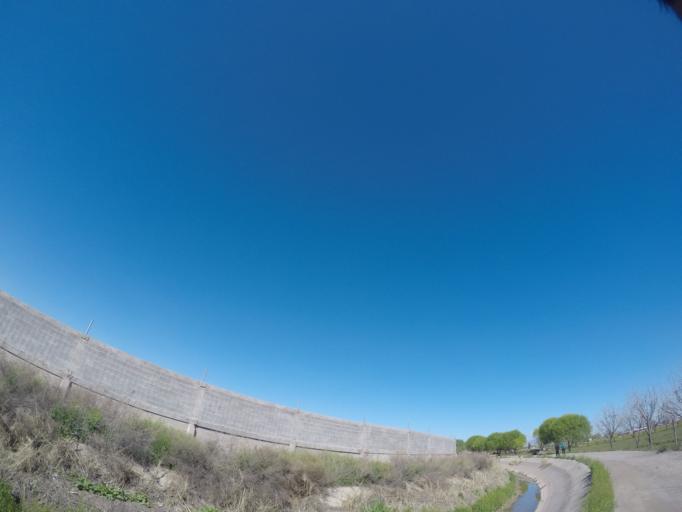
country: US
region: Texas
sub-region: El Paso County
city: Socorro
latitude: 31.6439
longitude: -106.3363
